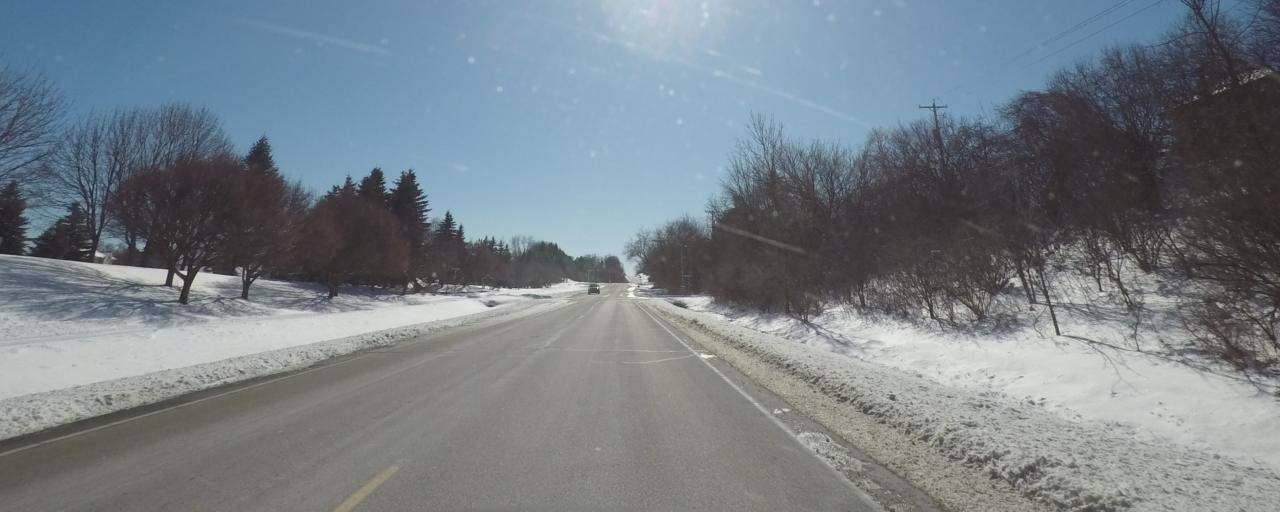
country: US
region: Wisconsin
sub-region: Waukesha County
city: Brookfield
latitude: 43.0280
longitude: -88.1468
